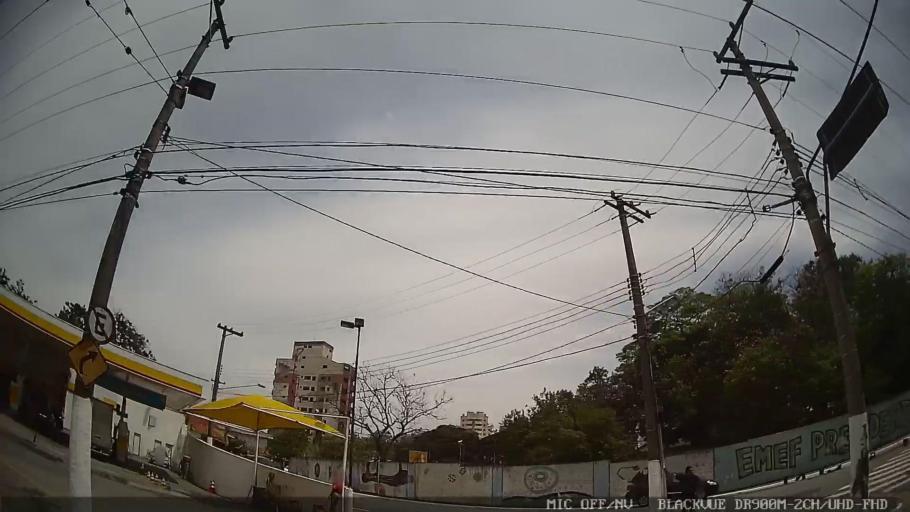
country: BR
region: Sao Paulo
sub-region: Sao Caetano Do Sul
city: Sao Caetano do Sul
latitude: -23.5630
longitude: -46.5523
